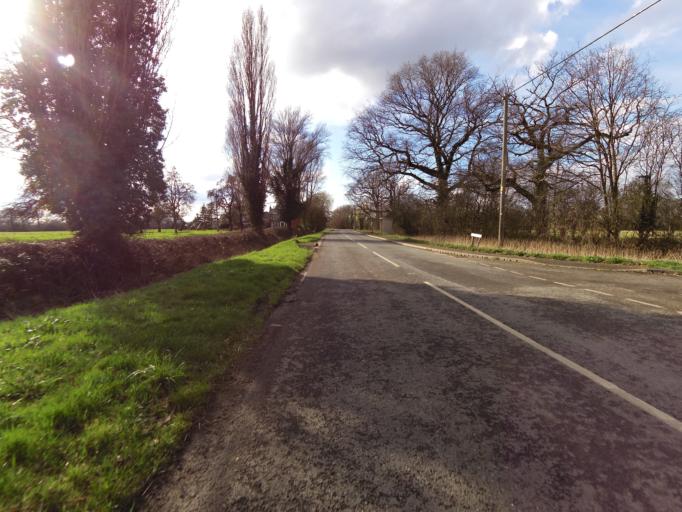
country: GB
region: England
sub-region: East Riding of Yorkshire
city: Pollington
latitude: 53.6480
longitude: -1.0364
